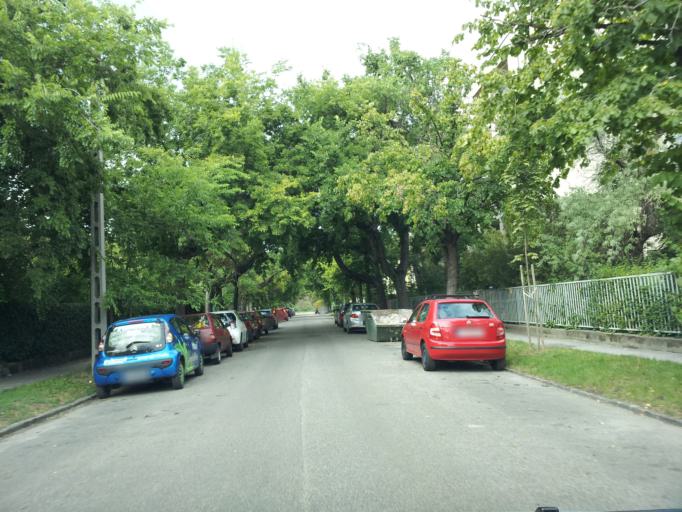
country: HU
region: Budapest
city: Budapest XI. keruelet
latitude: 47.4699
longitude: 19.0430
